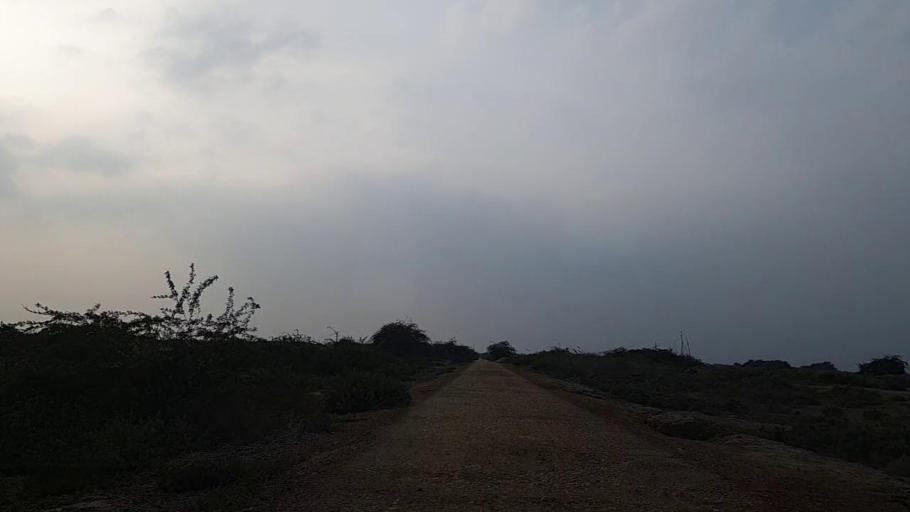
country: PK
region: Sindh
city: Mirpur Sakro
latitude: 24.6142
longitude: 67.5133
